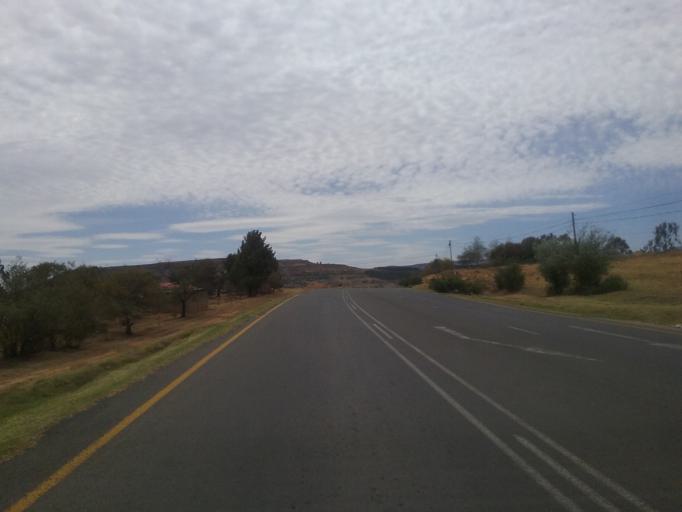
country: LS
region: Maseru
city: Nako
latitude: -29.6275
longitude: 27.4870
